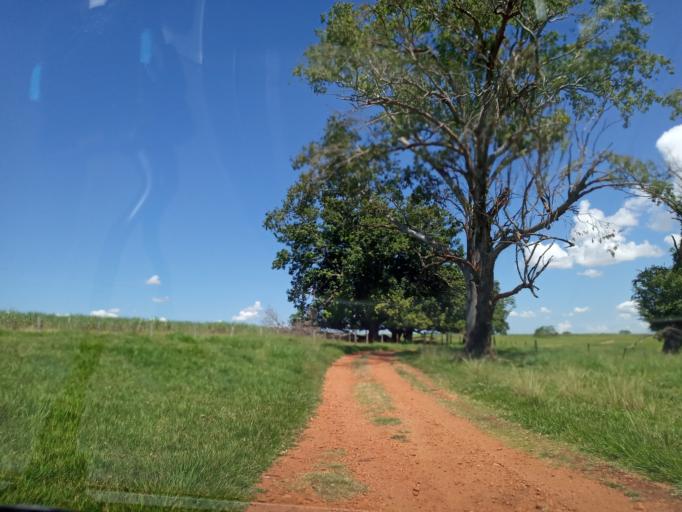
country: BR
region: Goias
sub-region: Itumbiara
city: Itumbiara
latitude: -18.3988
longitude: -49.1267
